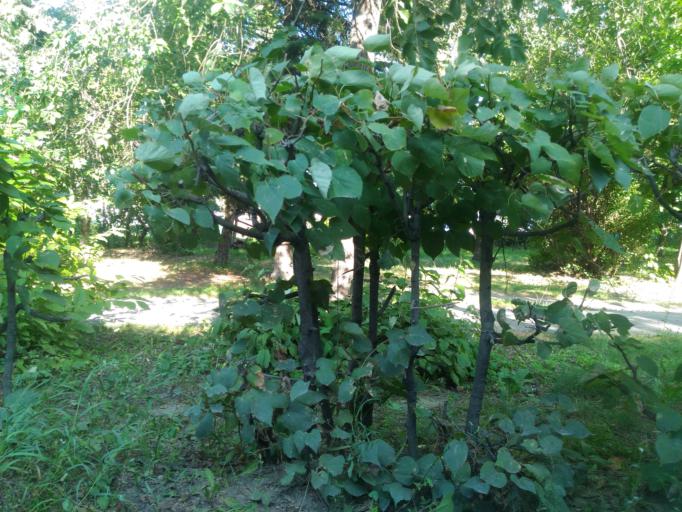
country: RU
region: Ulyanovsk
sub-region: Ulyanovskiy Rayon
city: Ulyanovsk
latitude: 54.3527
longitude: 48.5434
